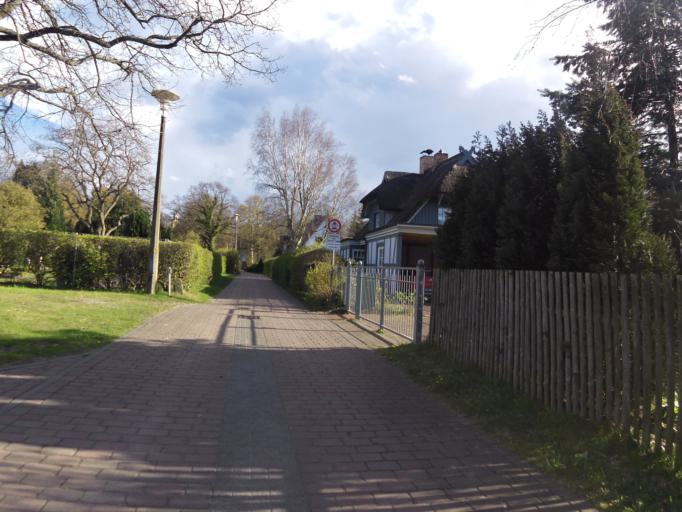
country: DE
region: Mecklenburg-Vorpommern
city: Zingst
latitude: 54.4393
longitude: 12.6882
